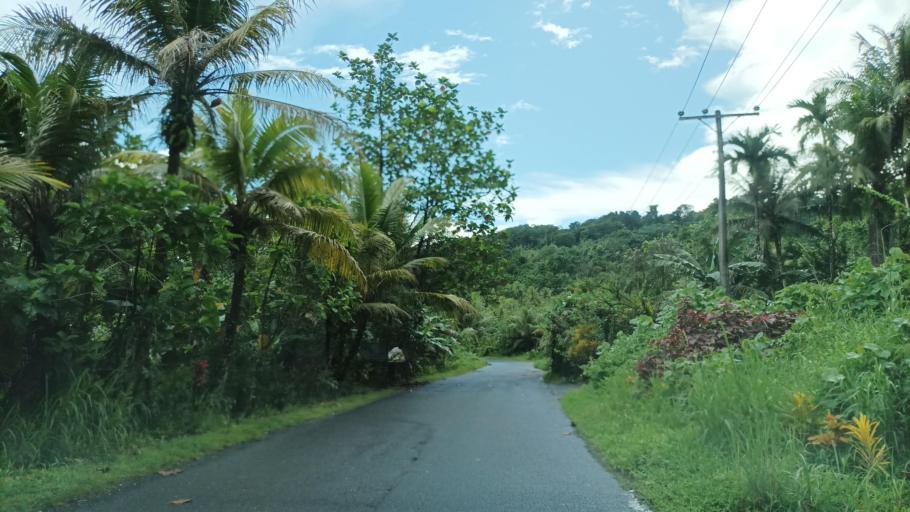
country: FM
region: Pohnpei
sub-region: Madolenihm Municipality
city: Madolenihm Municipality Government
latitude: 6.9138
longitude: 158.3001
